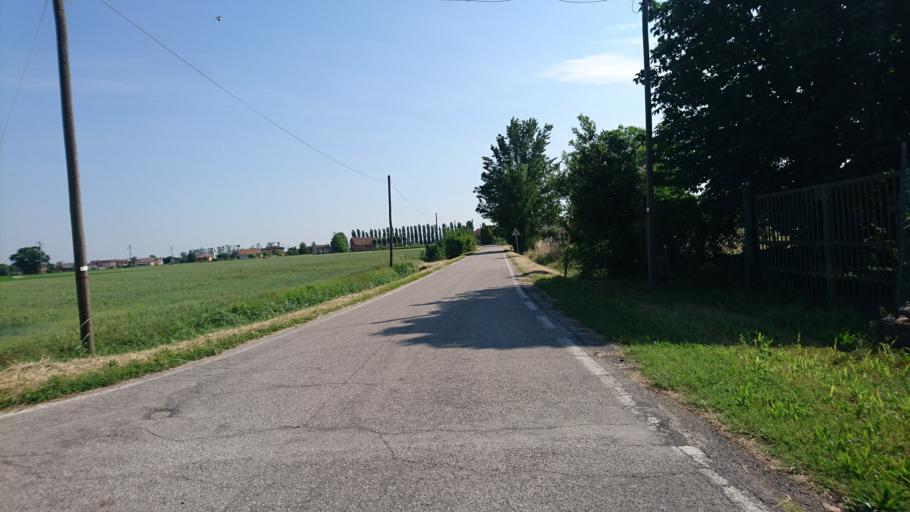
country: IT
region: Veneto
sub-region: Provincia di Padova
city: Merlara
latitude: 45.1729
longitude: 11.4634
